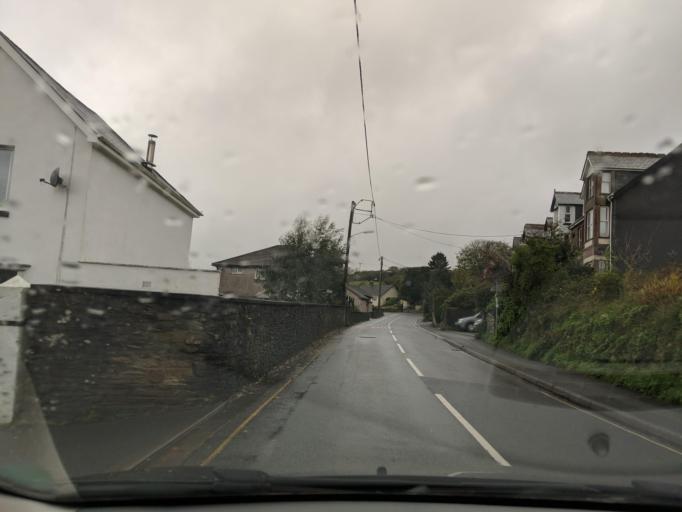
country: GB
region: England
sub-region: Cornwall
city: Bodmin
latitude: 50.4639
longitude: -4.7168
